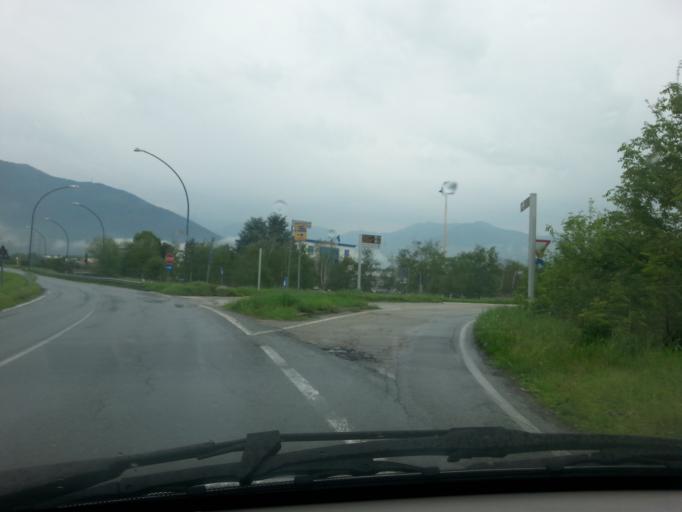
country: IT
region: Piedmont
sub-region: Provincia di Torino
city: Alpignano
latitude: 45.1025
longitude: 7.5114
